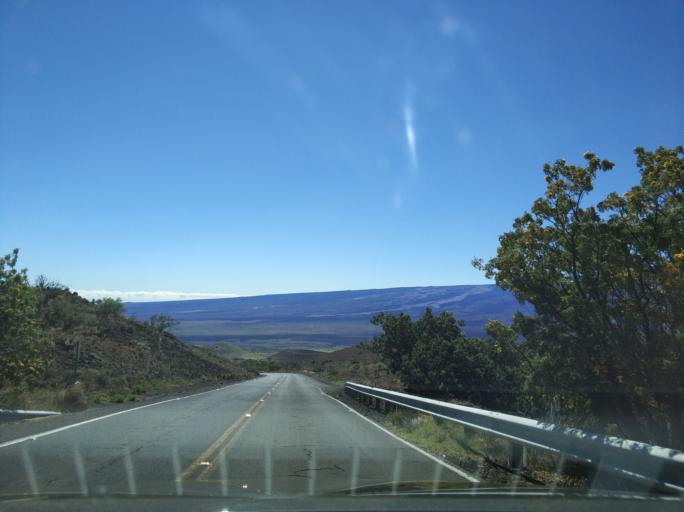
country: US
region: Hawaii
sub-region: Hawaii County
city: Honoka'a
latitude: 19.7500
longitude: -155.4549
